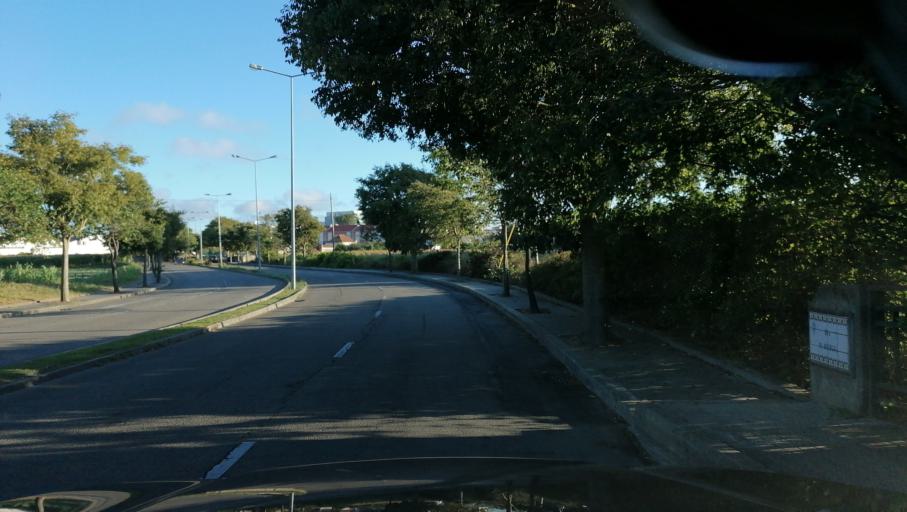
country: PT
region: Aveiro
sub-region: Aveiro
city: Aveiro
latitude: 40.6338
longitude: -8.6436
